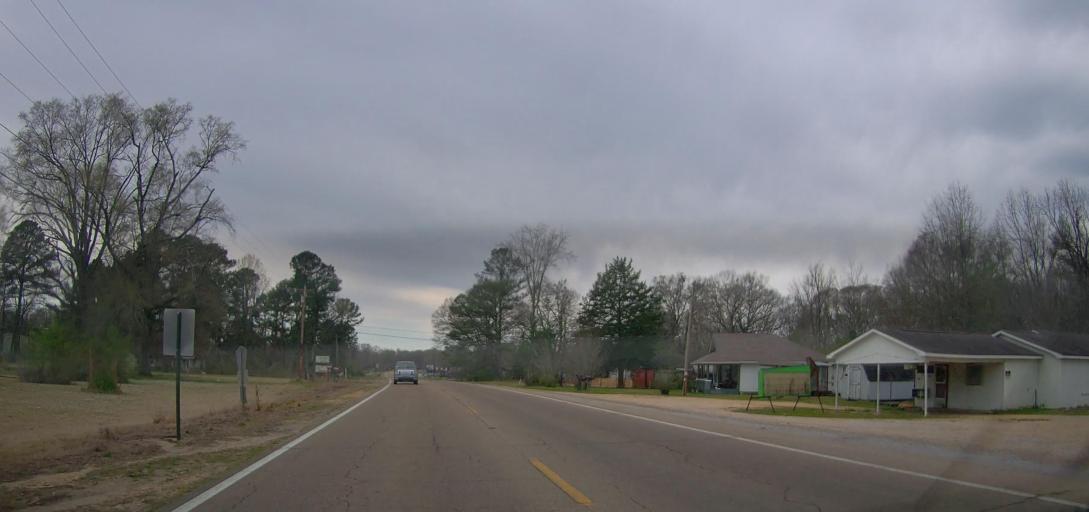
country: US
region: Mississippi
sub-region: Lee County
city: Plantersville
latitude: 34.2632
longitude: -88.6429
